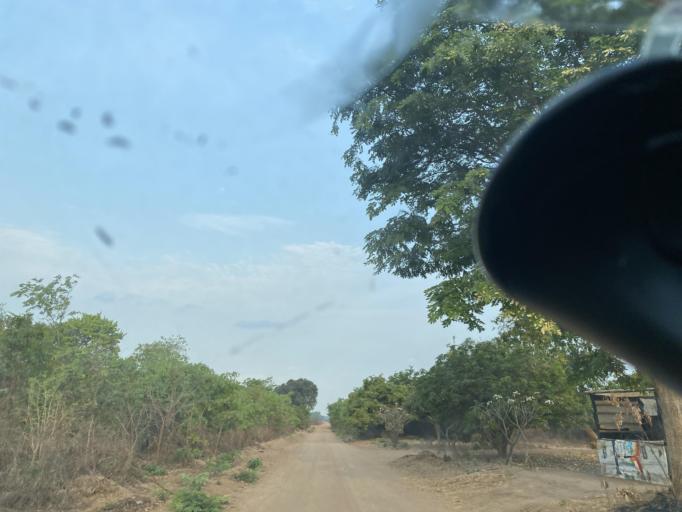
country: ZM
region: Lusaka
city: Chongwe
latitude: -15.2024
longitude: 28.5256
